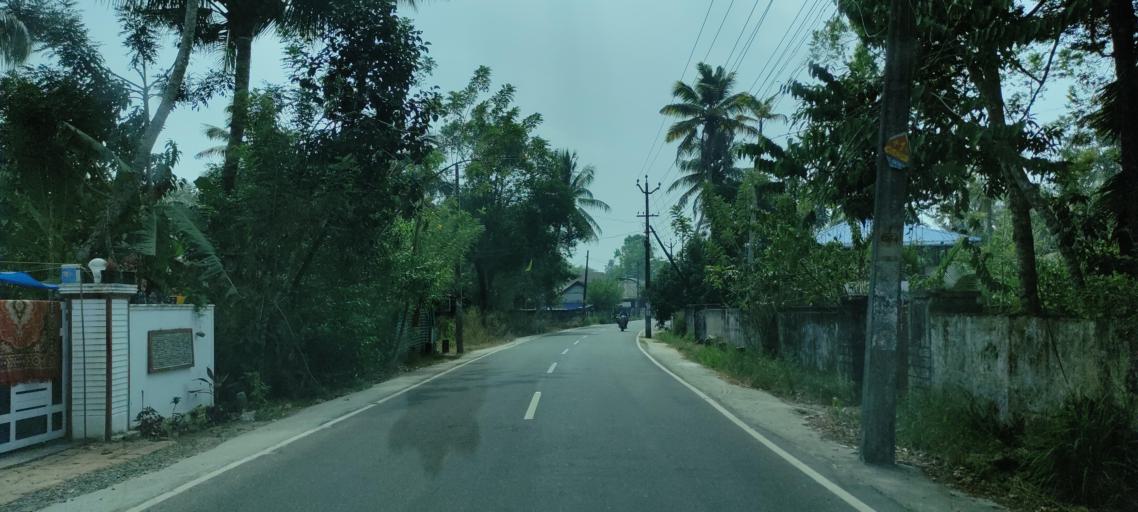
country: IN
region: Kerala
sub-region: Alappuzha
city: Shertallai
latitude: 9.5950
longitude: 76.3401
